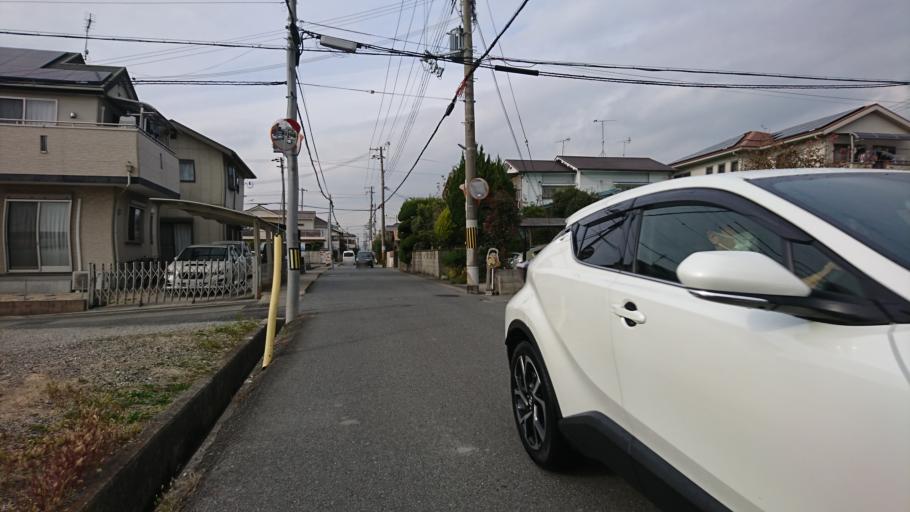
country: JP
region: Hyogo
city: Kakogawacho-honmachi
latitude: 34.7666
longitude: 134.8552
